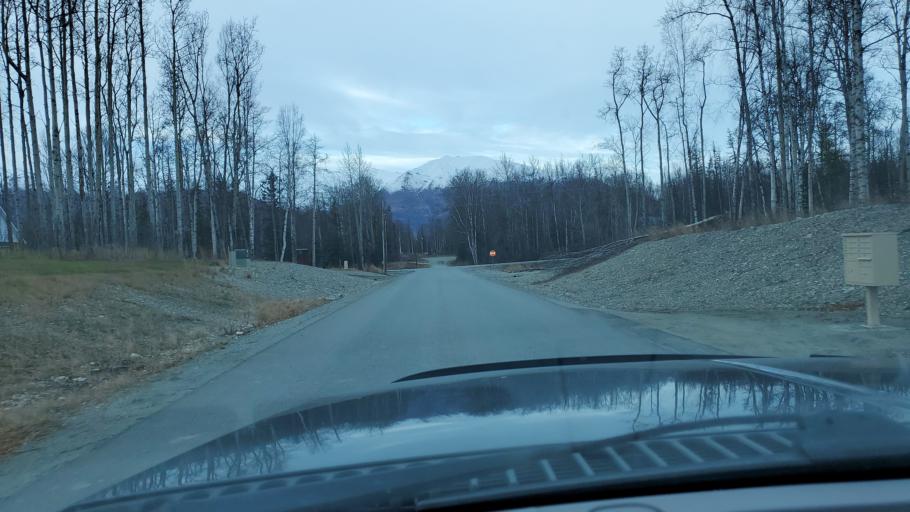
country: US
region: Alaska
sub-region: Matanuska-Susitna Borough
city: Lakes
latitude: 61.6562
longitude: -149.3036
